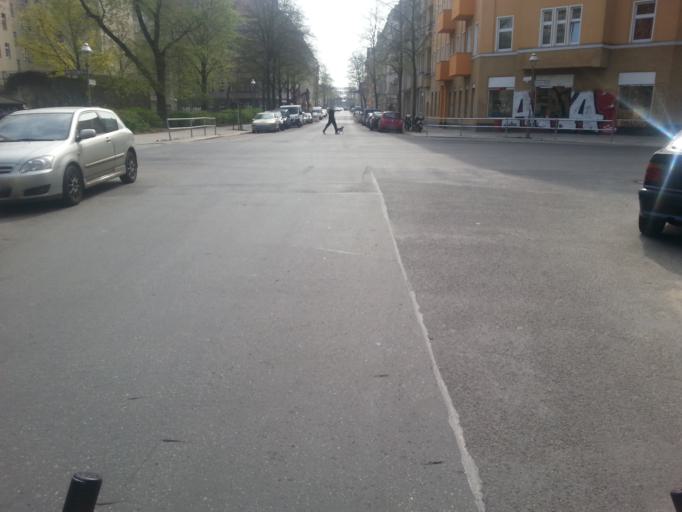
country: DE
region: Berlin
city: Berlin Treptow
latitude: 52.4707
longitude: 13.4352
